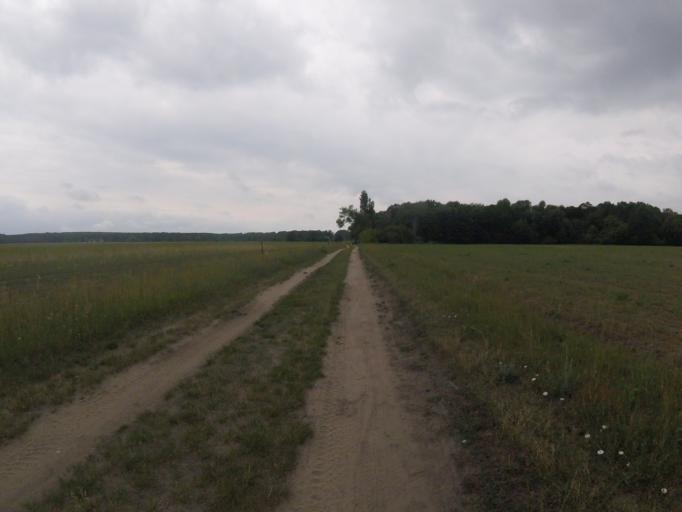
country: DE
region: Brandenburg
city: Bestensee
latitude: 52.2372
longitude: 13.6788
